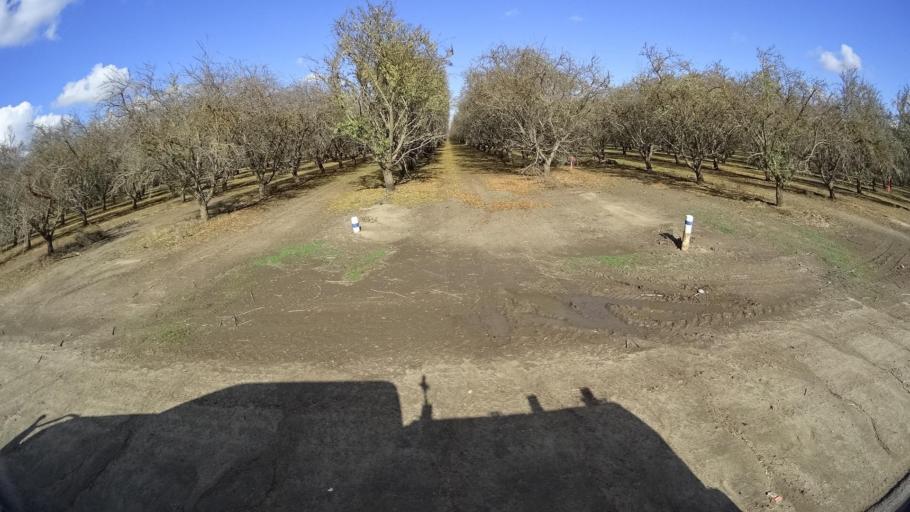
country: US
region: California
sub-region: Kern County
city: McFarland
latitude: 35.6742
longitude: -119.3061
